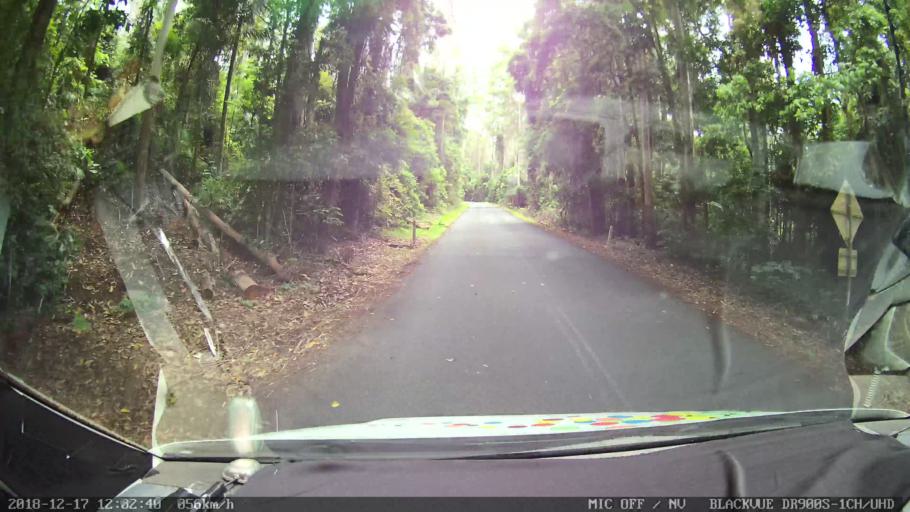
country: AU
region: New South Wales
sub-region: Kyogle
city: Kyogle
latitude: -28.5141
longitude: 152.5690
